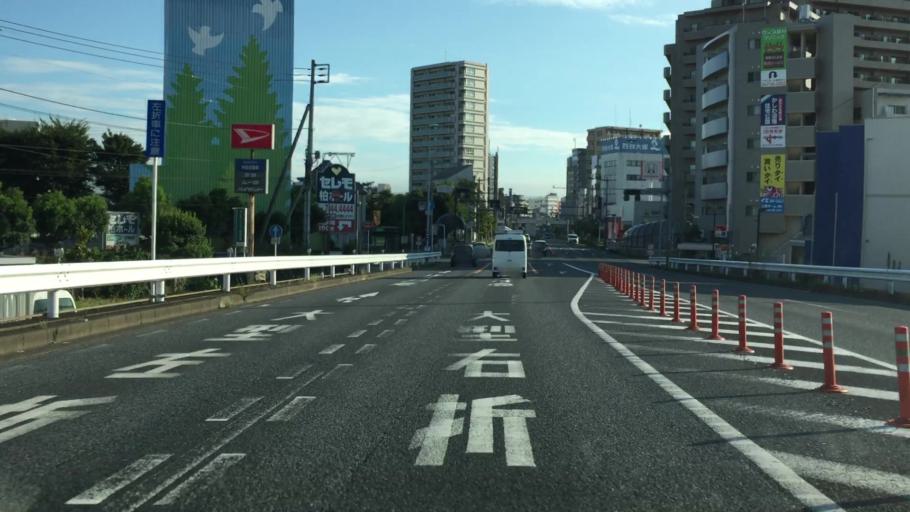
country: JP
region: Chiba
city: Kashiwa
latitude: 35.8596
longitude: 139.9658
